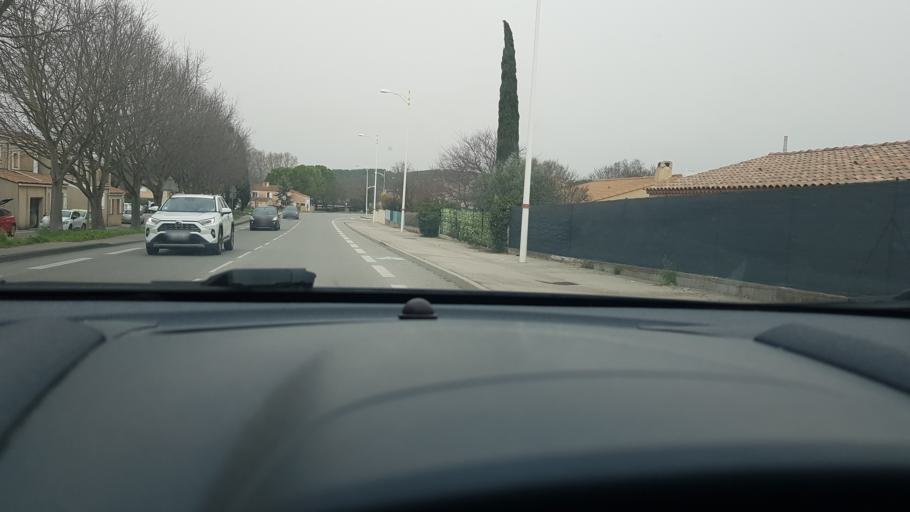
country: FR
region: Provence-Alpes-Cote d'Azur
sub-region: Departement des Bouches-du-Rhone
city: Gardanne
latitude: 43.4470
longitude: 5.4731
